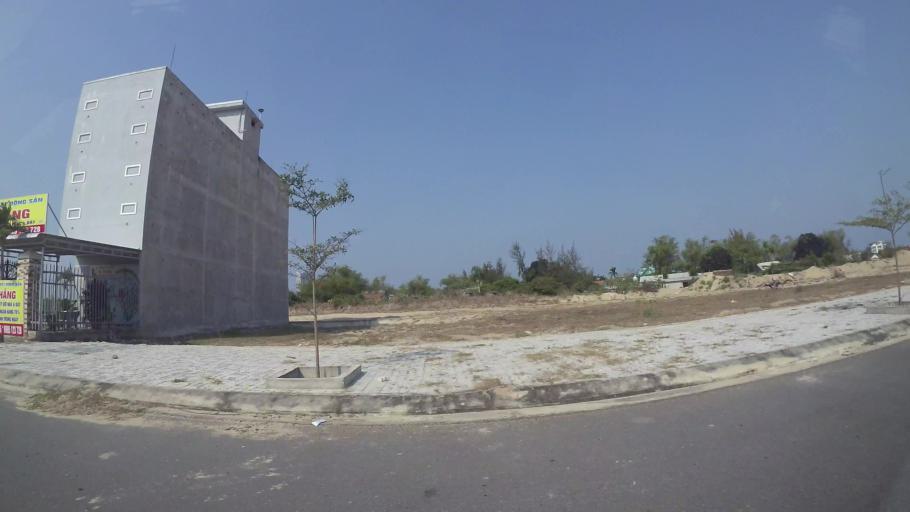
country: VN
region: Da Nang
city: Ngu Hanh Son
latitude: 15.9558
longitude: 108.2771
